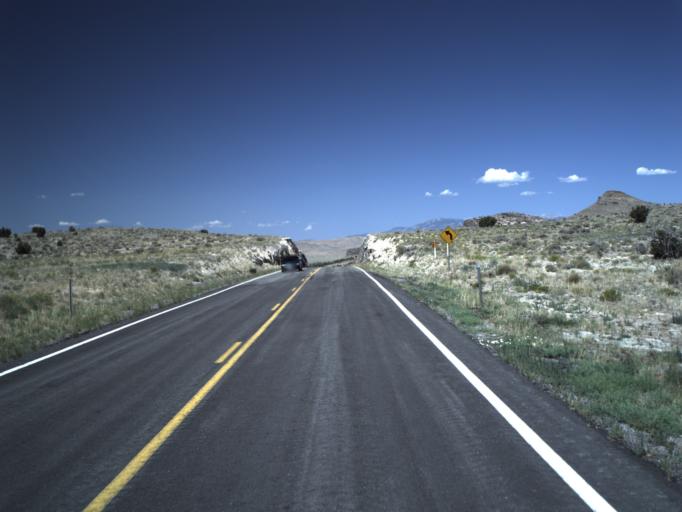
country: US
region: Utah
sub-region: Beaver County
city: Milford
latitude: 39.0783
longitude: -113.6944
